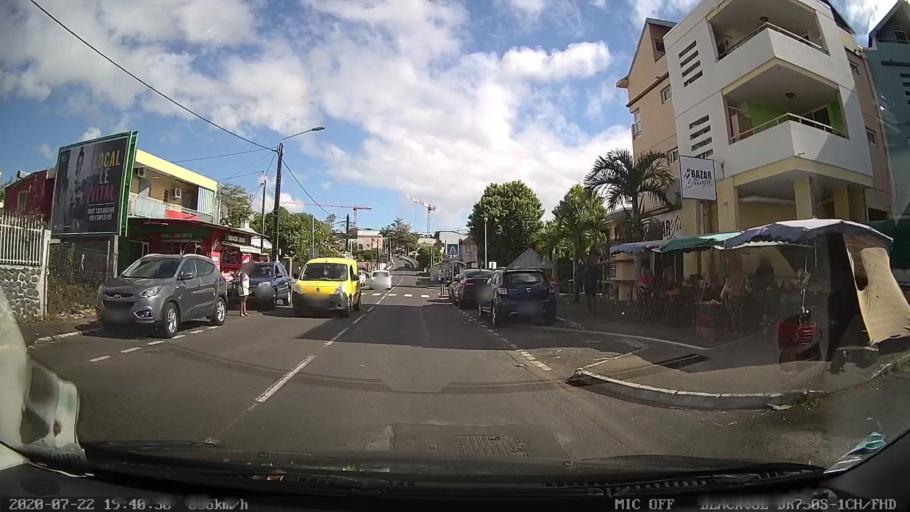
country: RE
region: Reunion
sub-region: Reunion
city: Sainte-Suzanne
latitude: -20.9052
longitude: 55.6063
